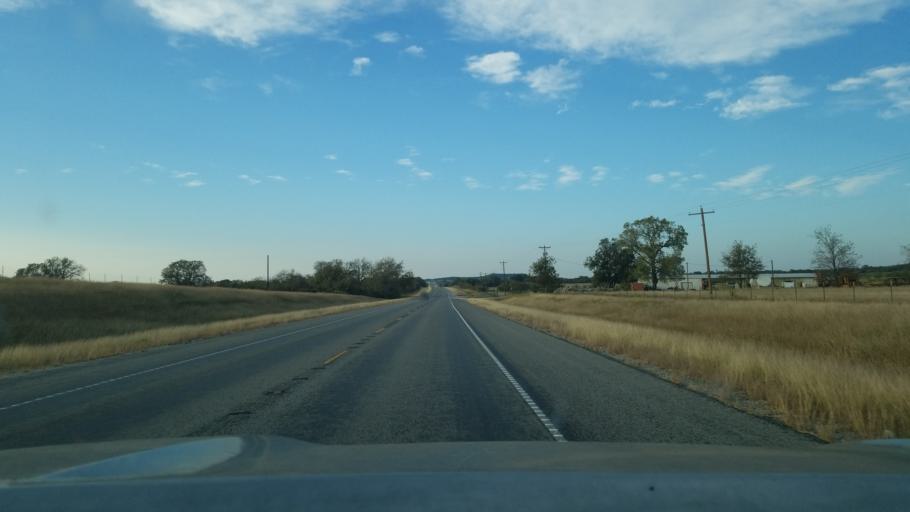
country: US
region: Texas
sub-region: Brown County
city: Lake Brownwood
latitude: 32.0364
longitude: -98.9351
